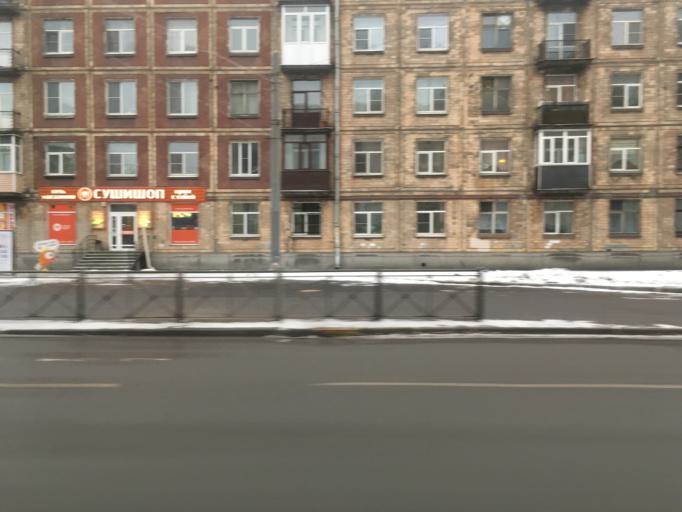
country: RU
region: St.-Petersburg
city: Obukhovo
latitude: 59.8736
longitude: 30.4368
